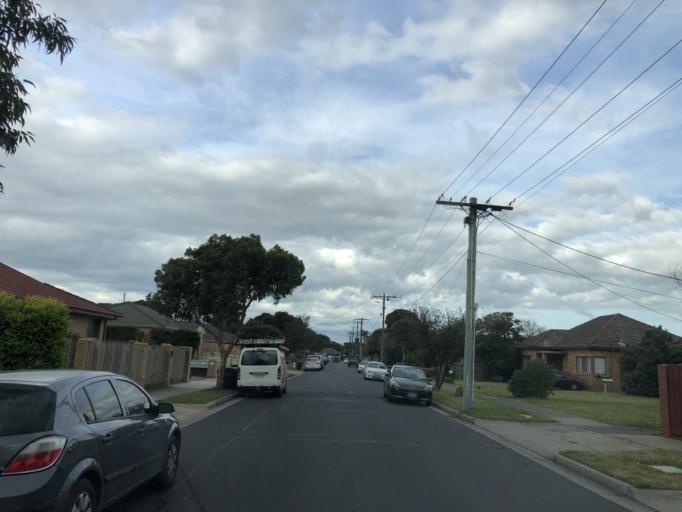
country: AU
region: Victoria
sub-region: Kingston
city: Bonbeach
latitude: -38.0608
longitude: 145.1233
